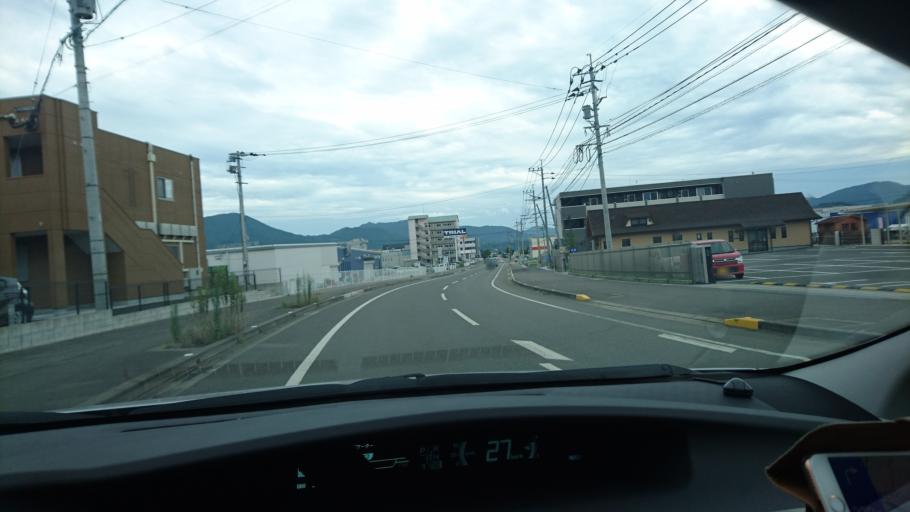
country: JP
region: Saga Prefecture
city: Takeocho-takeo
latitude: 33.2012
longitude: 130.0330
